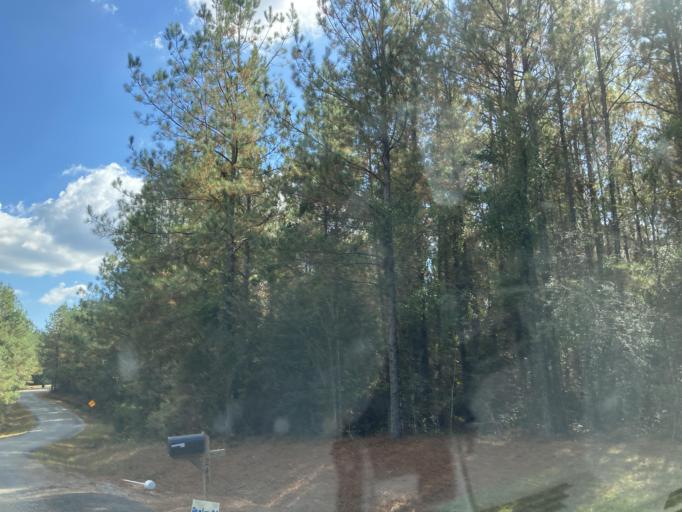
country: US
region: Mississippi
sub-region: Lamar County
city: Sumrall
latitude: 31.3731
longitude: -89.5425
